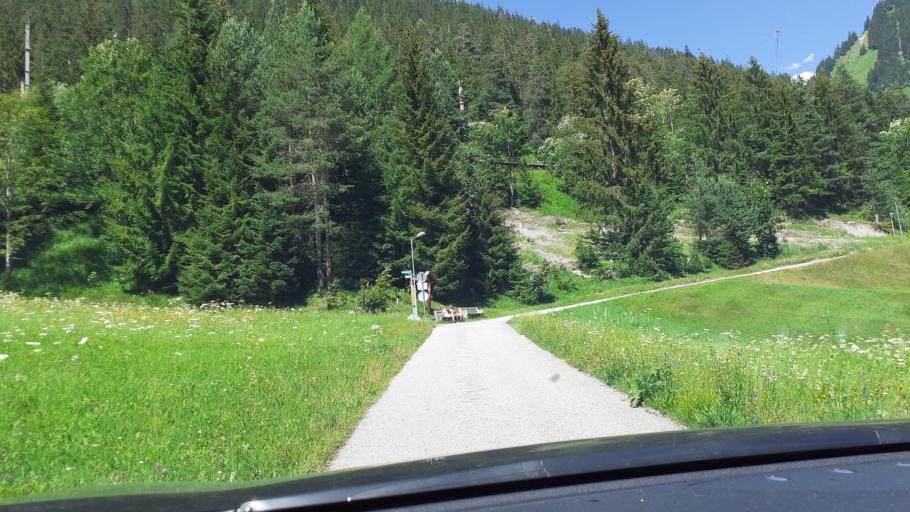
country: AT
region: Vorarlberg
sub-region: Politischer Bezirk Bludenz
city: Klosterle
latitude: 47.1335
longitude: 10.0501
